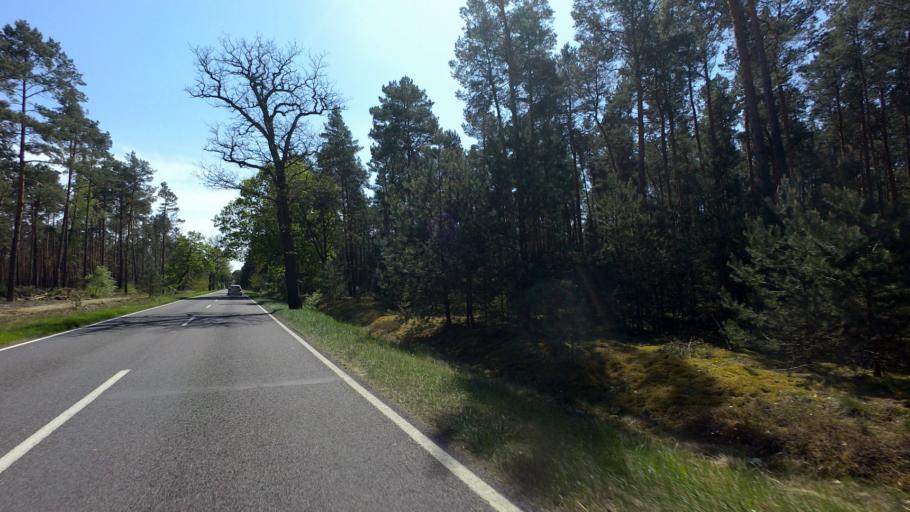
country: DE
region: Brandenburg
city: Gross Koris
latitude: 52.1711
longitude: 13.7218
